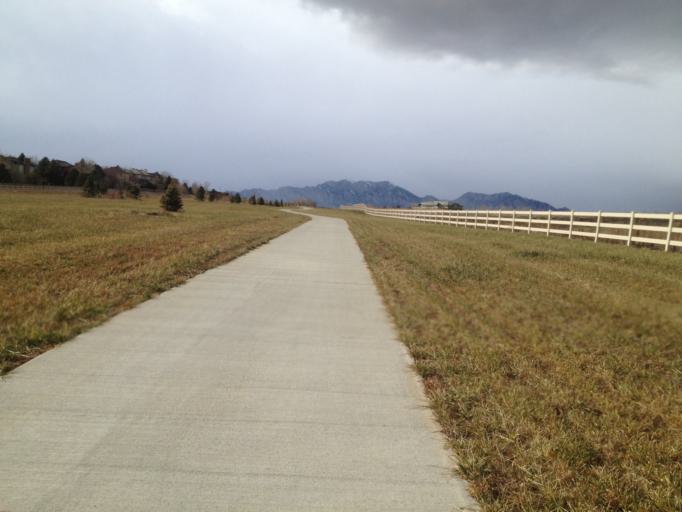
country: US
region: Colorado
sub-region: Boulder County
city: Superior
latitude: 39.9473
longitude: -105.1554
